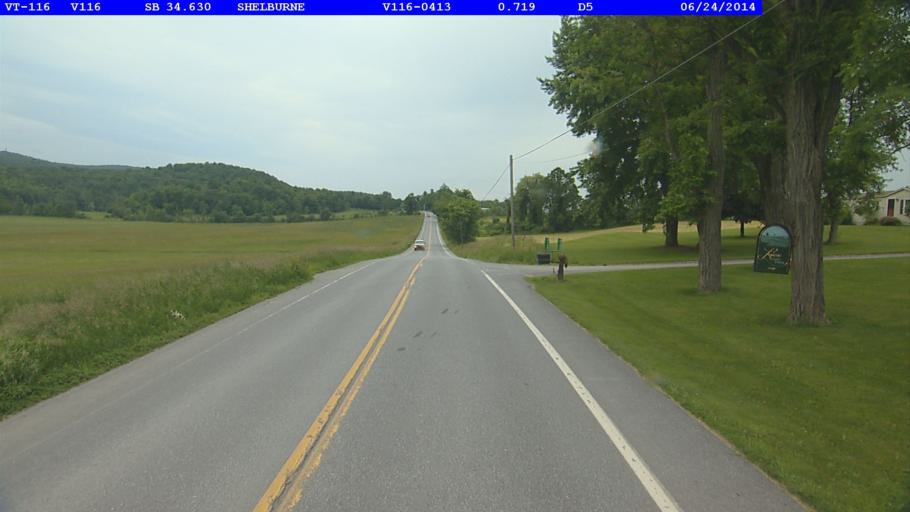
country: US
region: Vermont
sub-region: Chittenden County
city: Hinesburg
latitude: 44.3892
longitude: -73.1422
